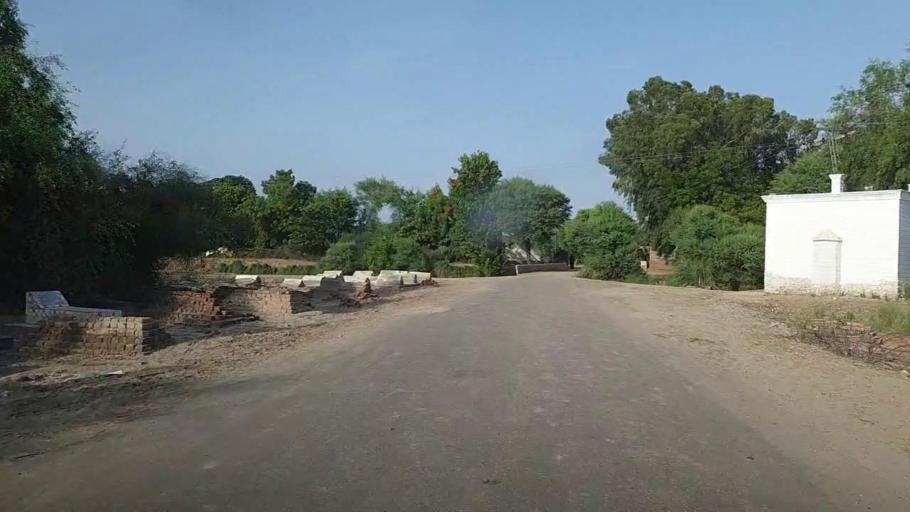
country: PK
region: Sindh
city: Ubauro
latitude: 28.1144
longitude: 69.8519
